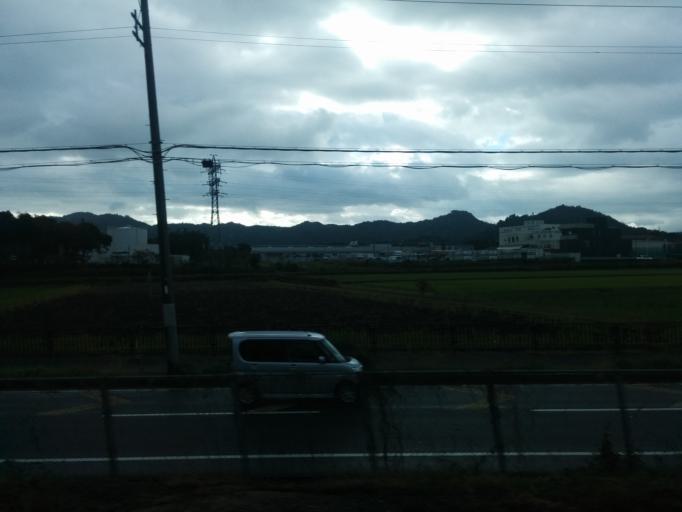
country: JP
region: Shiga Prefecture
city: Moriyama
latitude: 35.0844
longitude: 136.0459
